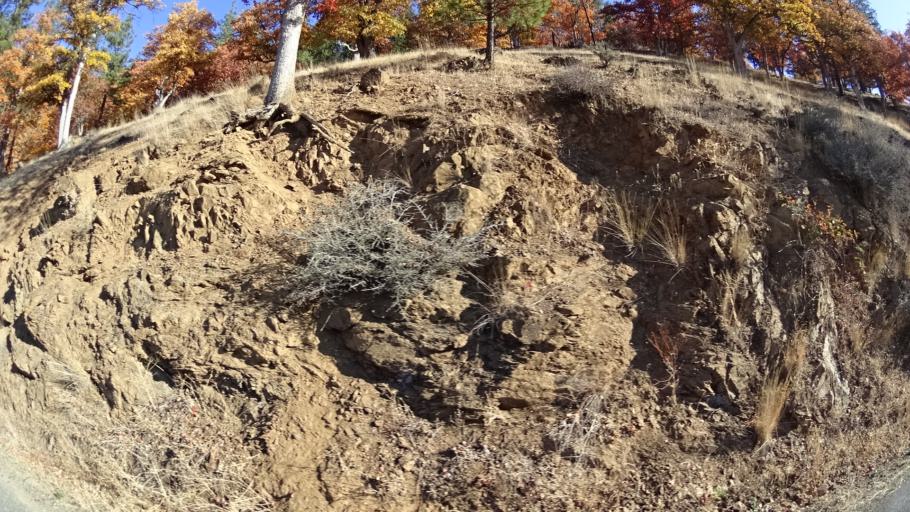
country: US
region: California
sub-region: Siskiyou County
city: Yreka
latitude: 41.6339
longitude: -122.9577
